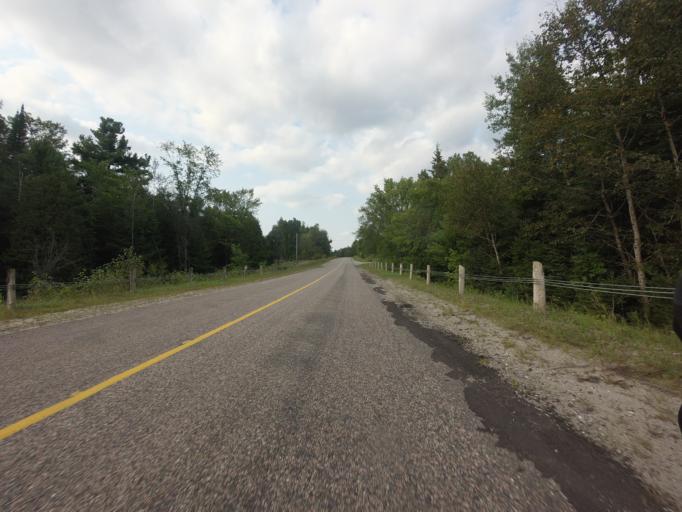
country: CA
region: Ontario
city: Perth
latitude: 44.8856
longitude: -76.6944
